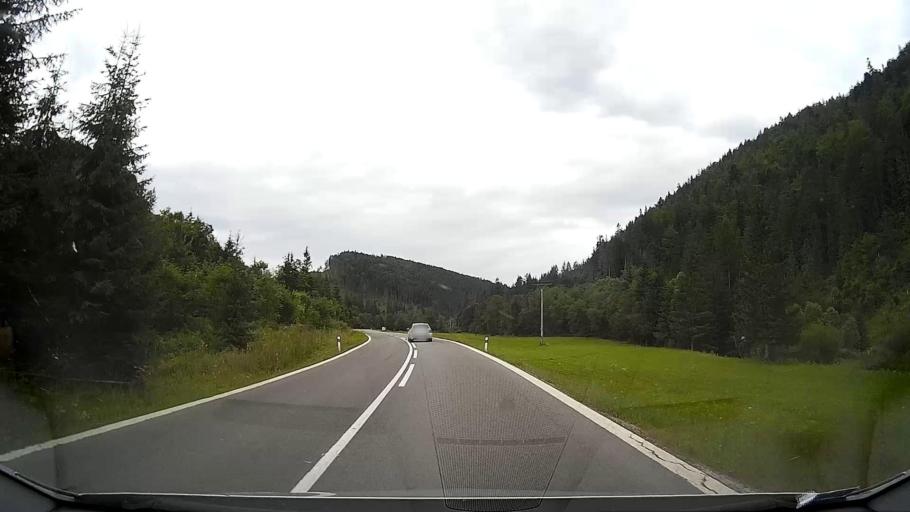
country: SK
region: Banskobystricky
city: Revuca
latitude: 48.8242
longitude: 20.1476
